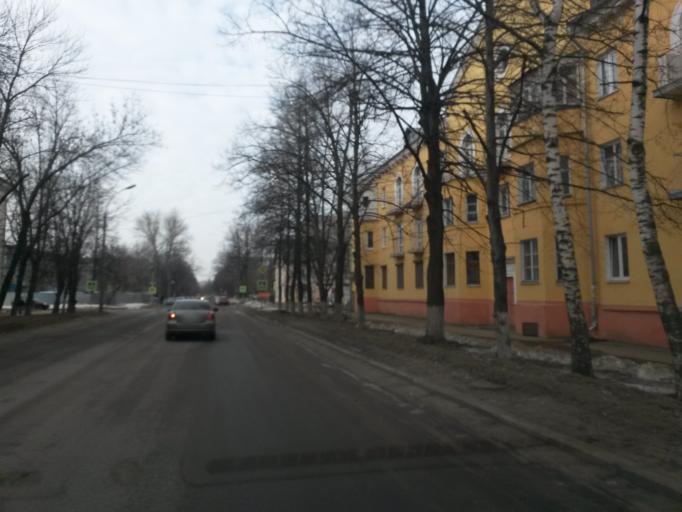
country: RU
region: Jaroslavl
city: Yaroslavl
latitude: 57.6341
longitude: 39.8455
